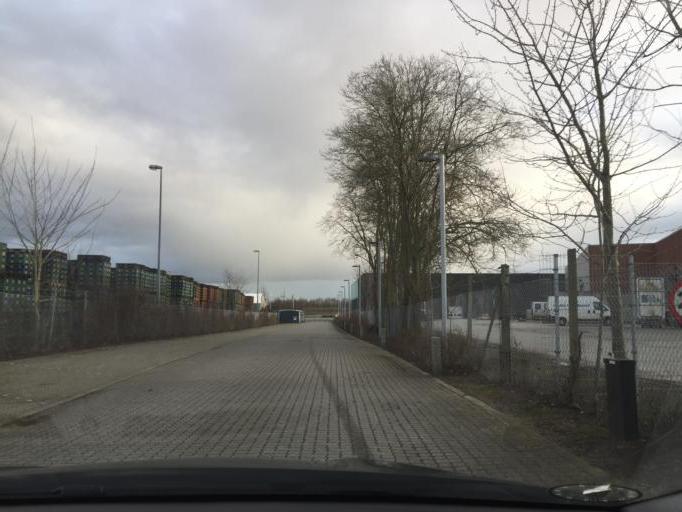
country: DK
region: South Denmark
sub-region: Odense Kommune
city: Hojby
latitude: 55.3540
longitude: 10.3967
